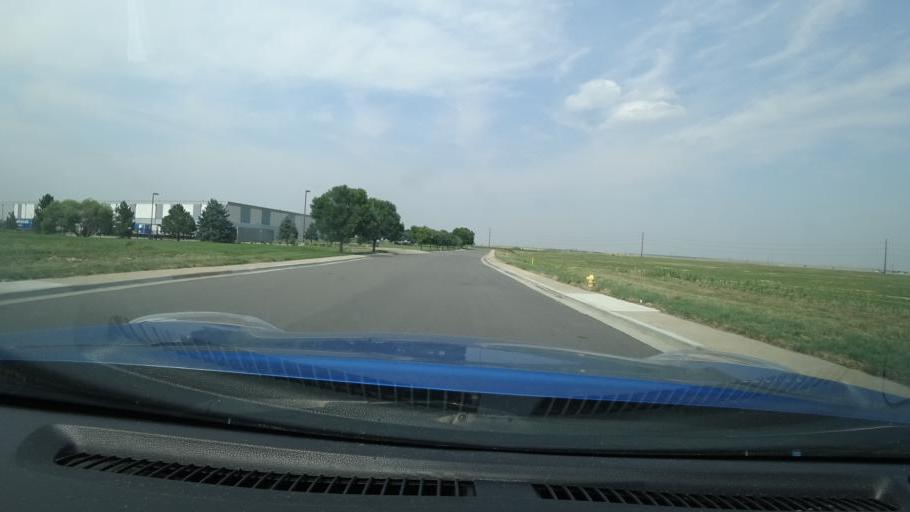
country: US
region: Colorado
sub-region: Adams County
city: Aurora
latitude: 39.7598
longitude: -104.7399
